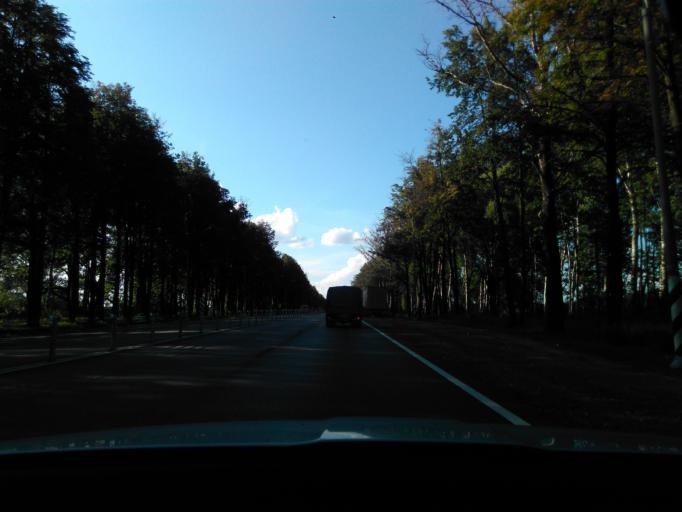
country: RU
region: Tverskaya
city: Zavidovo
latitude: 56.5653
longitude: 36.5049
